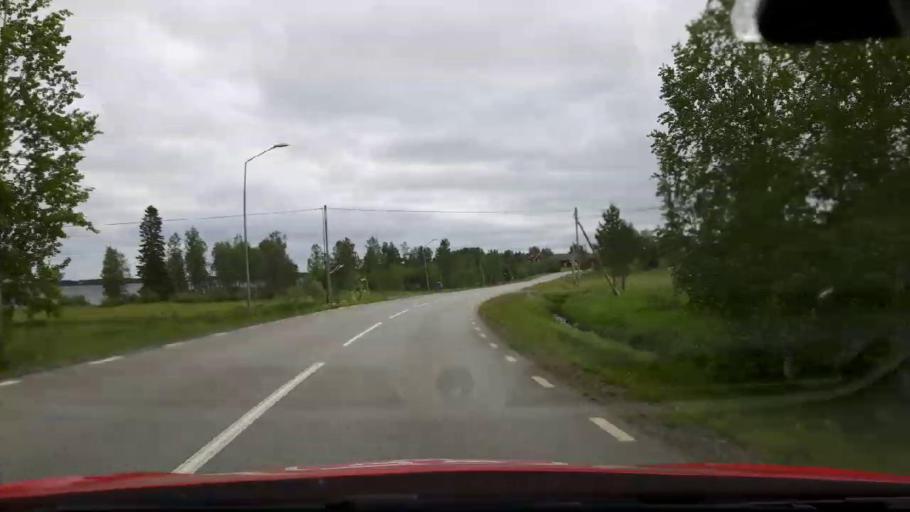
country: SE
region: Jaemtland
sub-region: OEstersunds Kommun
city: Lit
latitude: 63.6813
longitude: 15.0399
